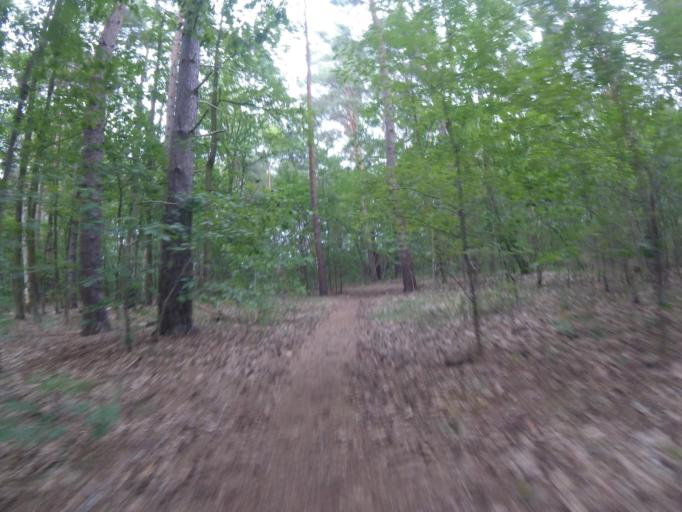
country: DE
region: Brandenburg
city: Gross Koris
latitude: 52.1699
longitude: 13.7028
